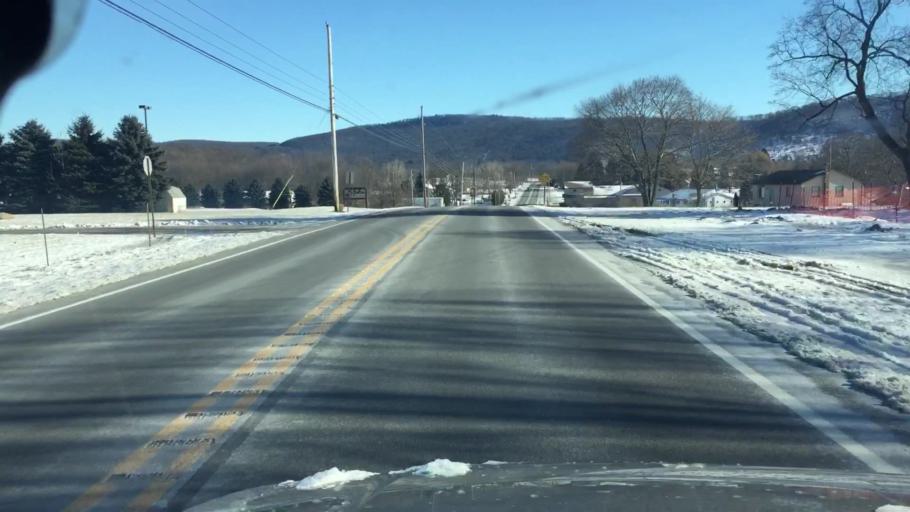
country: US
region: Pennsylvania
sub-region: Luzerne County
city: Nescopeck
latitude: 41.0471
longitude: -76.1493
